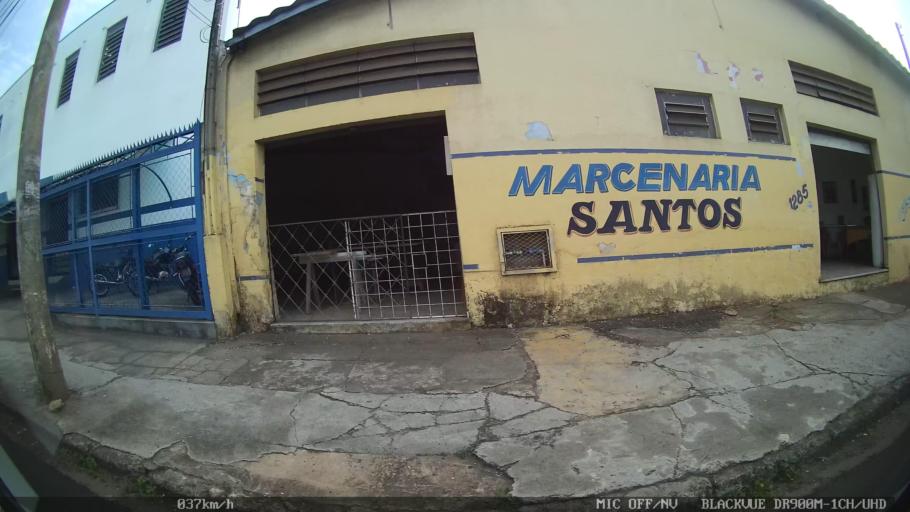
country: BR
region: Sao Paulo
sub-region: Piracicaba
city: Piracicaba
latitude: -22.7425
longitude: -47.6306
